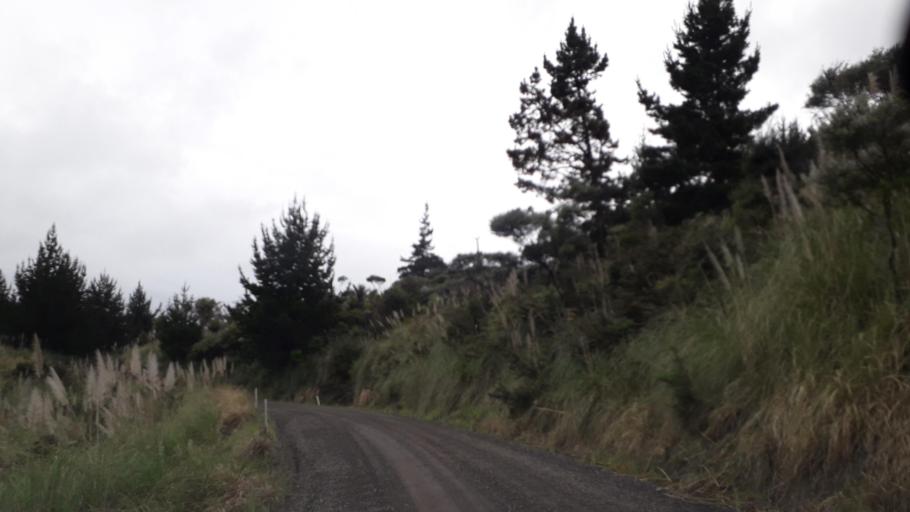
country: NZ
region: Northland
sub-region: Far North District
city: Kaitaia
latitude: -35.3711
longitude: 173.4118
